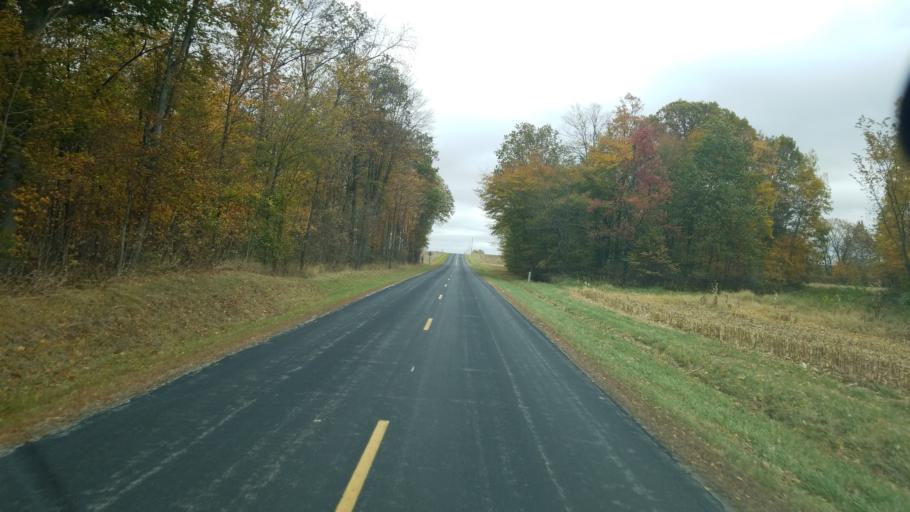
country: US
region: Ohio
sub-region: Crawford County
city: Bucyrus
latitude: 40.9172
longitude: -82.8521
